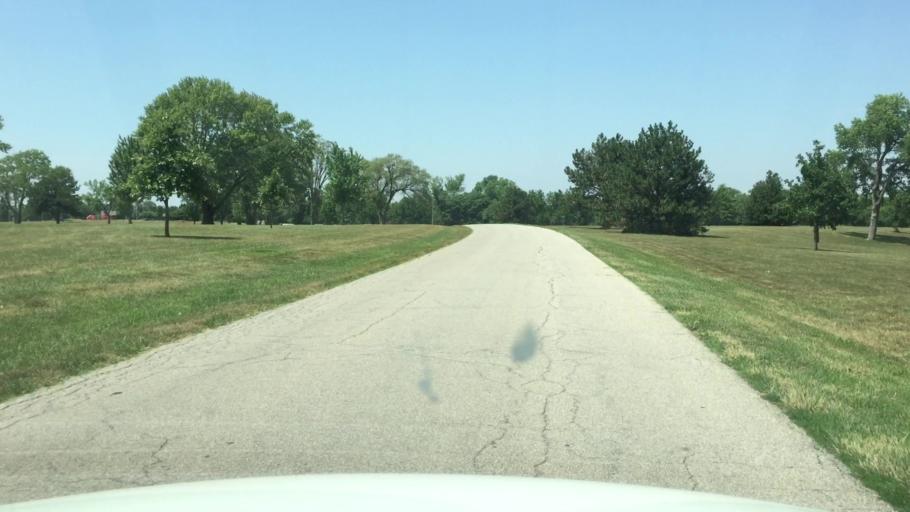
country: US
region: Kansas
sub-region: Shawnee County
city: Topeka
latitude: 39.0072
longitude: -95.6171
